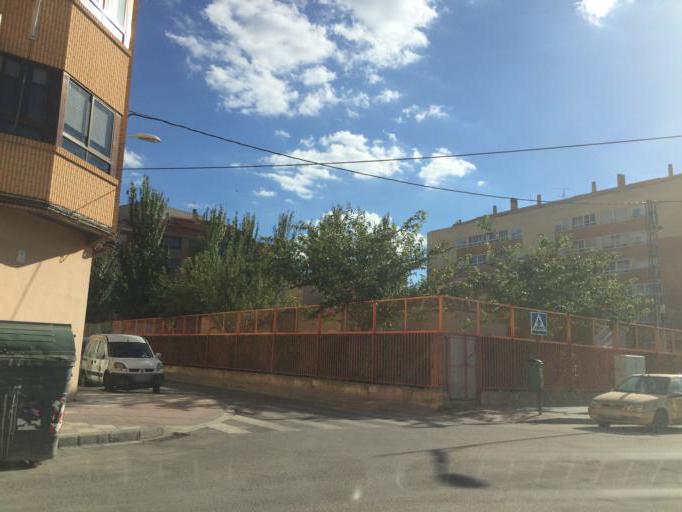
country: ES
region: Castille-La Mancha
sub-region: Provincia de Albacete
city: Albacete
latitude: 38.9942
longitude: -1.8769
